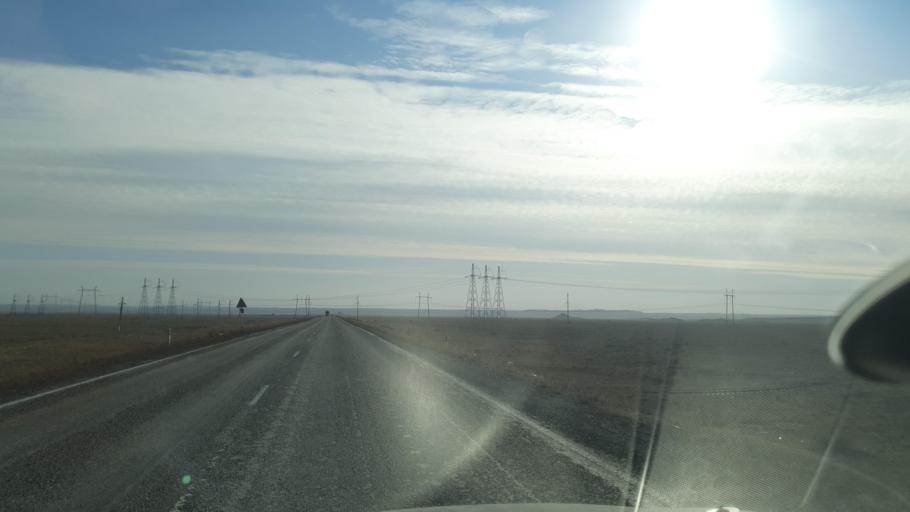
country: KZ
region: Zhambyl
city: Mynaral
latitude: 45.6044
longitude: 73.3979
